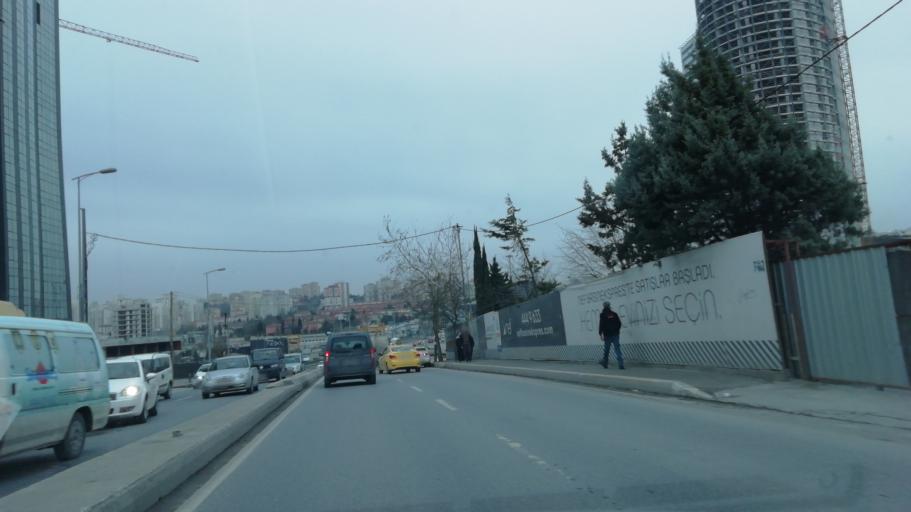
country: TR
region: Istanbul
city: Mahmutbey
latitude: 41.0453
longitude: 28.8128
